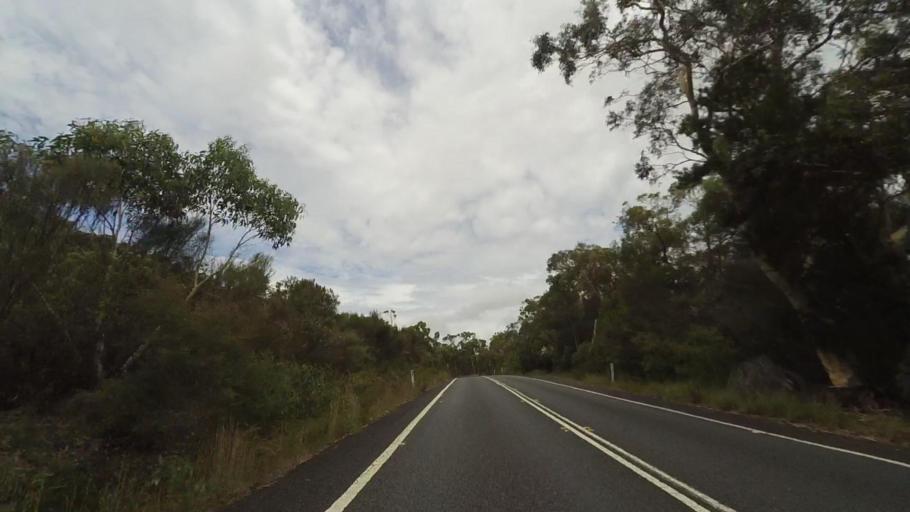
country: AU
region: New South Wales
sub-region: Sutherland Shire
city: Grays Point
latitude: -34.1178
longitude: 151.0698
